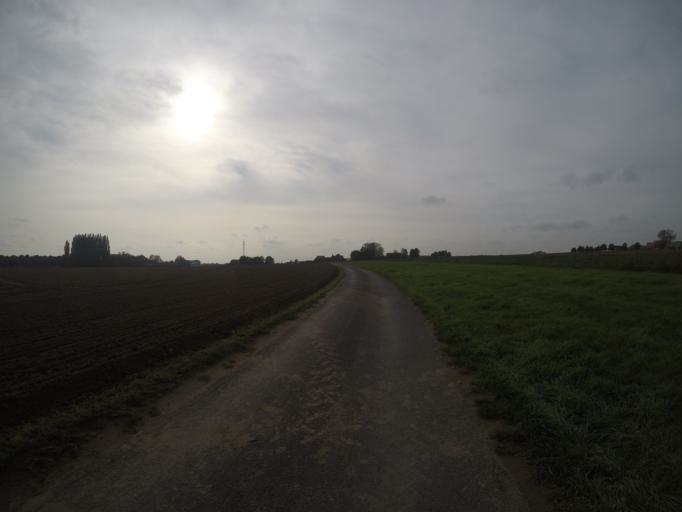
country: BE
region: Flanders
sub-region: Provincie West-Vlaanderen
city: Moorslede
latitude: 50.8343
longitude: 3.0695
